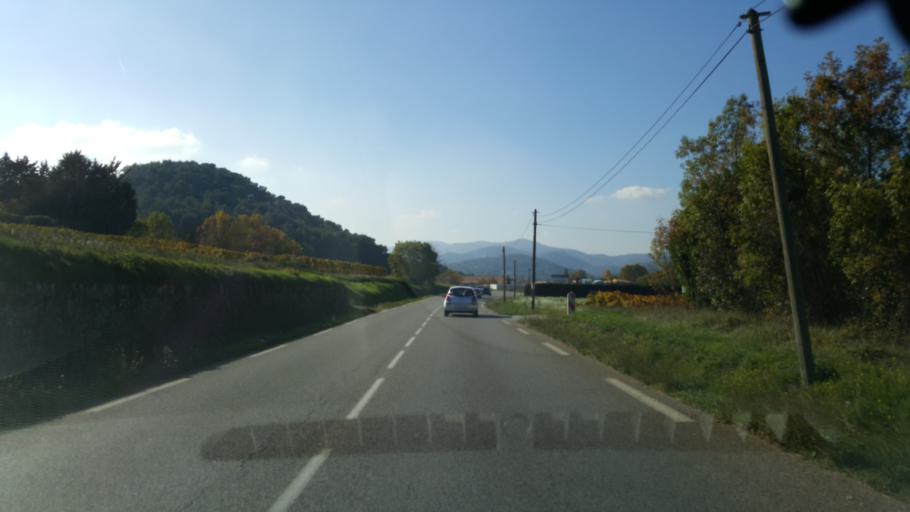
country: FR
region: Provence-Alpes-Cote d'Azur
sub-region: Departement des Bouches-du-Rhone
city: Auriol
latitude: 43.3704
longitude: 5.6618
